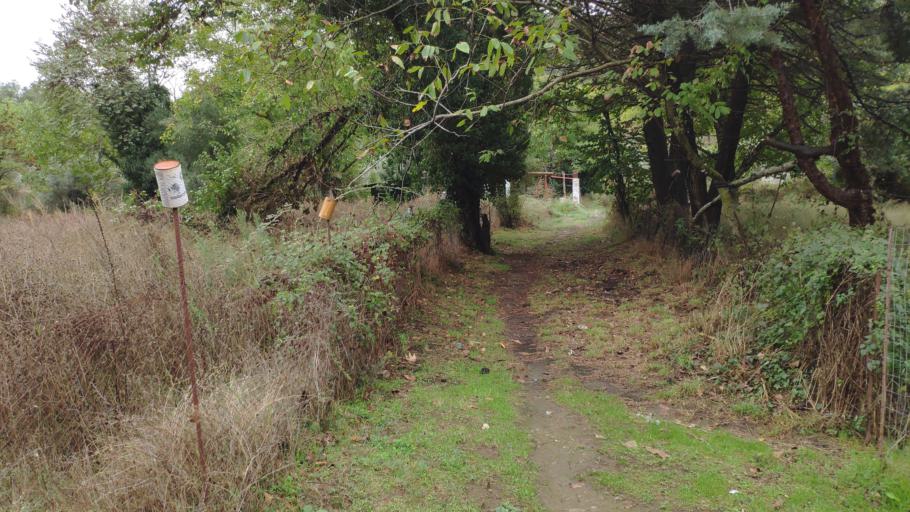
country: GR
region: West Greece
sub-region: Nomos Aitolias kai Akarnanias
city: Sardinia
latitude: 38.9259
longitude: 21.3574
